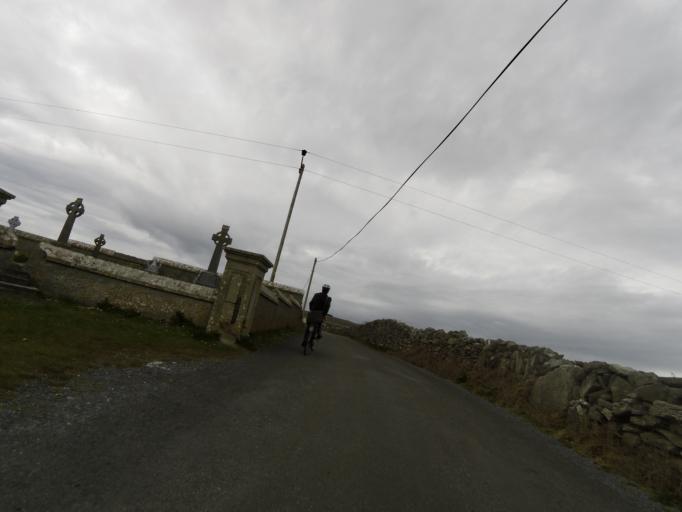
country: IE
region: Connaught
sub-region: County Galway
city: Clifden
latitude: 53.1315
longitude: -9.7532
